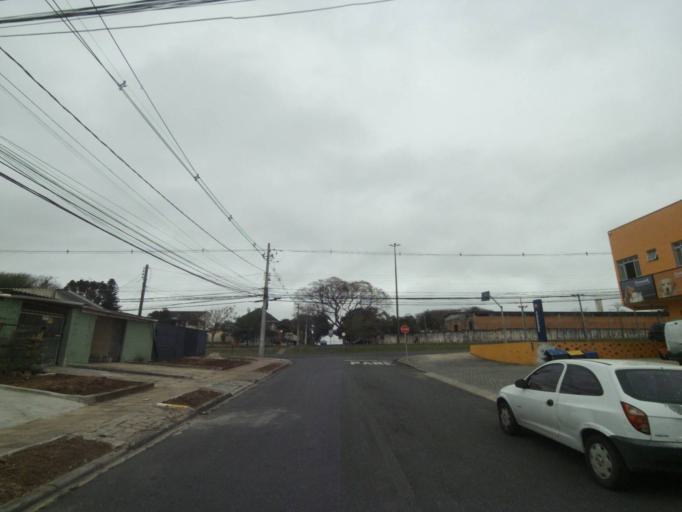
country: BR
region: Parana
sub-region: Curitiba
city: Curitiba
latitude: -25.4735
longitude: -49.2709
